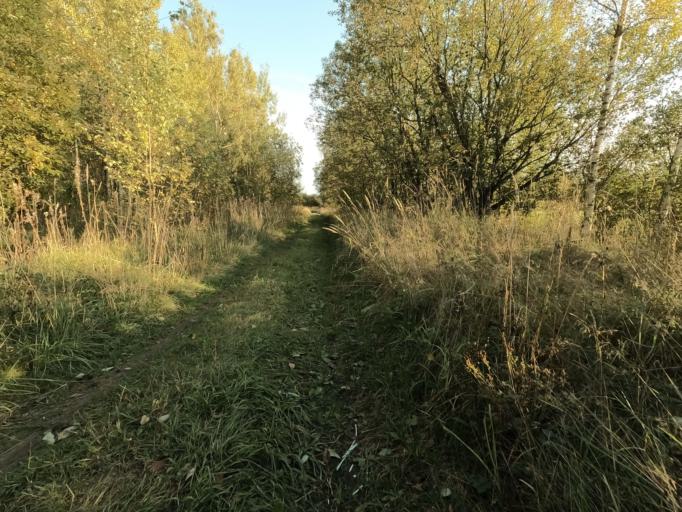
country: RU
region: Leningrad
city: Nikol'skoye
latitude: 59.7016
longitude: 30.7389
